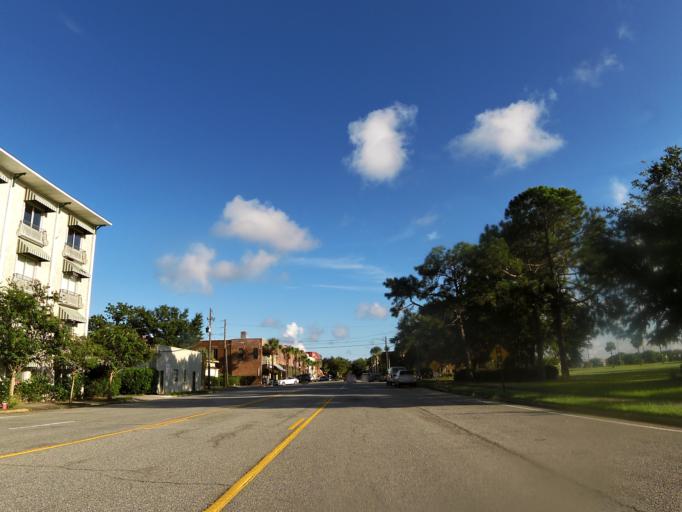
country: US
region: Georgia
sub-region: Glynn County
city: Brunswick
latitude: 31.1525
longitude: -81.4966
